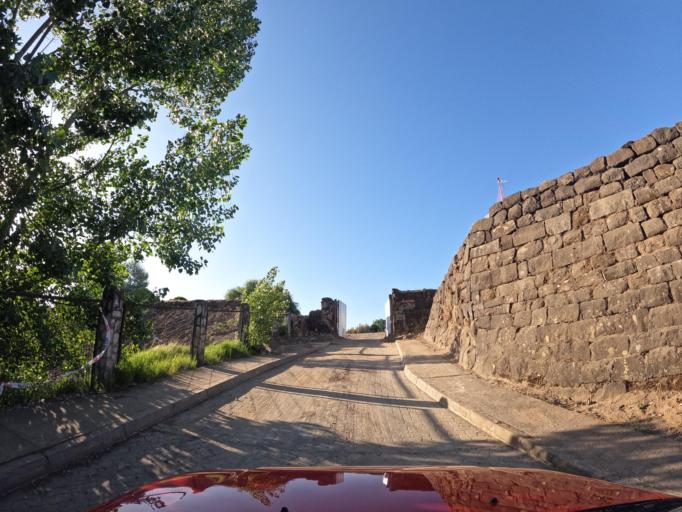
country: CL
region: Biobio
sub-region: Provincia de Concepcion
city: Lota
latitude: -37.1695
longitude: -72.9406
